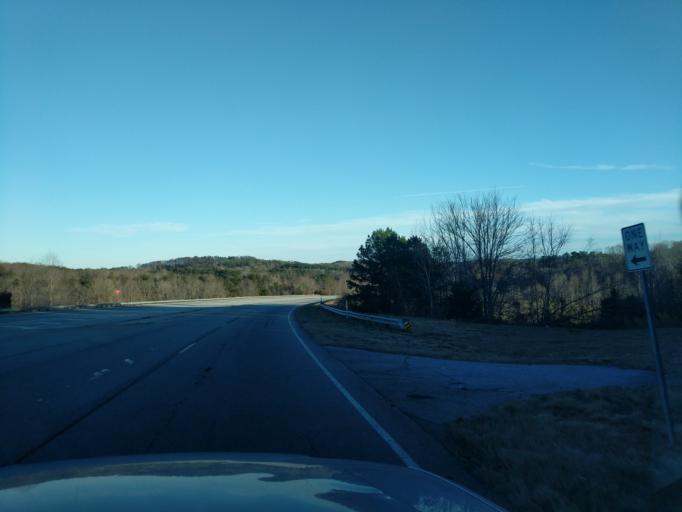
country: US
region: Georgia
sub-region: Stephens County
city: Toccoa
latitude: 34.5528
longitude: -83.3744
